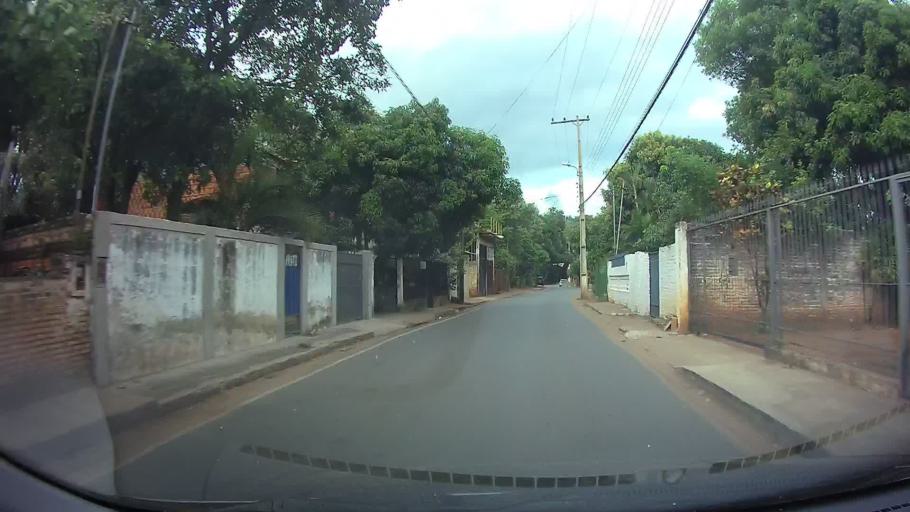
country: PY
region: Central
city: Fernando de la Mora
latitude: -25.3026
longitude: -57.5214
